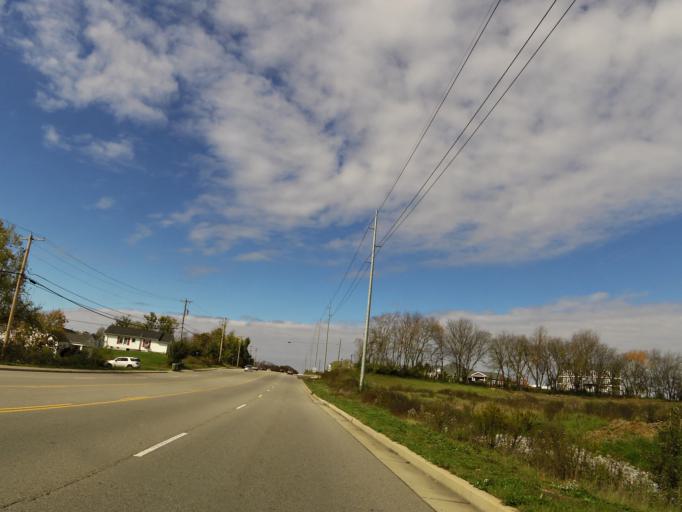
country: US
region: Tennessee
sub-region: Blount County
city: Maryville
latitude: 35.7651
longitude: -83.9917
